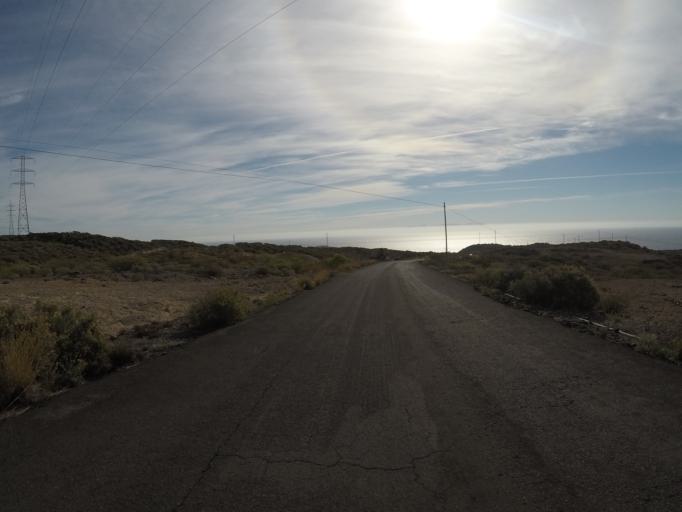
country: ES
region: Canary Islands
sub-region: Provincia de Santa Cruz de Tenerife
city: Lomo de Arico
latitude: 28.1256
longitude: -16.4723
